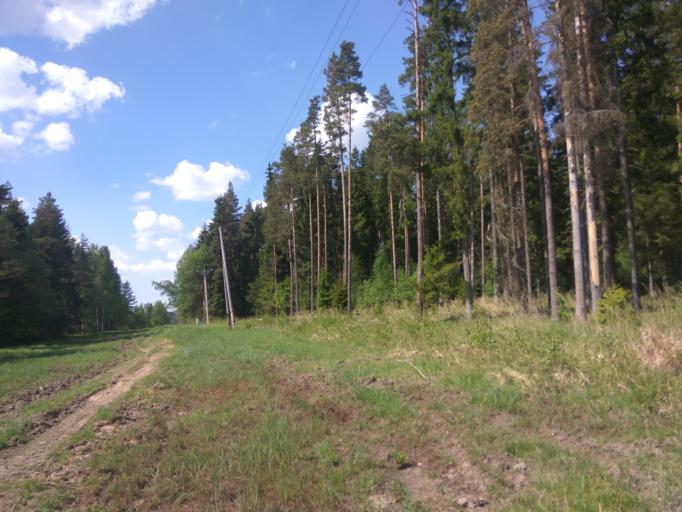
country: LV
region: Kuldigas Rajons
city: Kuldiga
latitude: 57.1862
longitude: 21.9911
